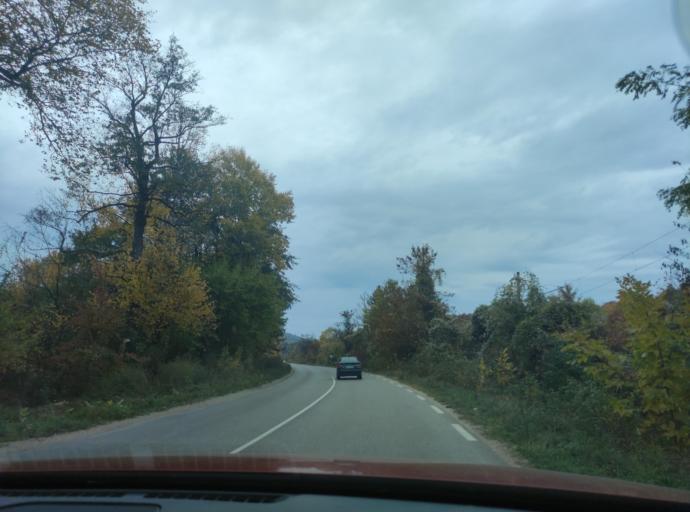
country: BG
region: Montana
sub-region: Obshtina Berkovitsa
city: Berkovitsa
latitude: 43.2673
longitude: 23.1752
